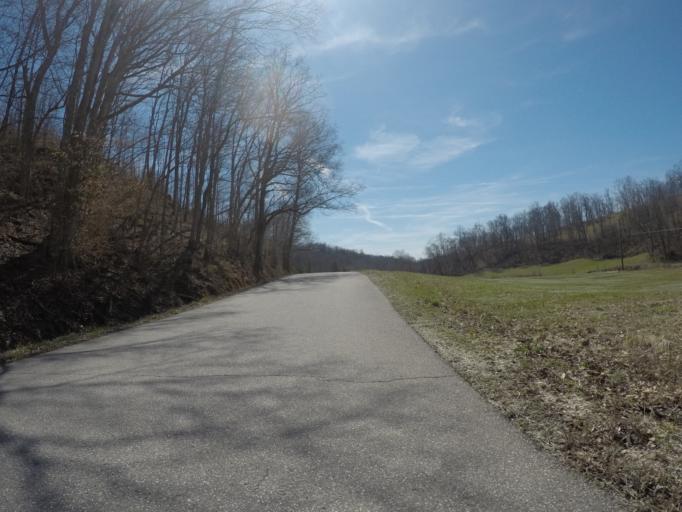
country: US
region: Ohio
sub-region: Lawrence County
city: South Point
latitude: 38.4763
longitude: -82.5659
